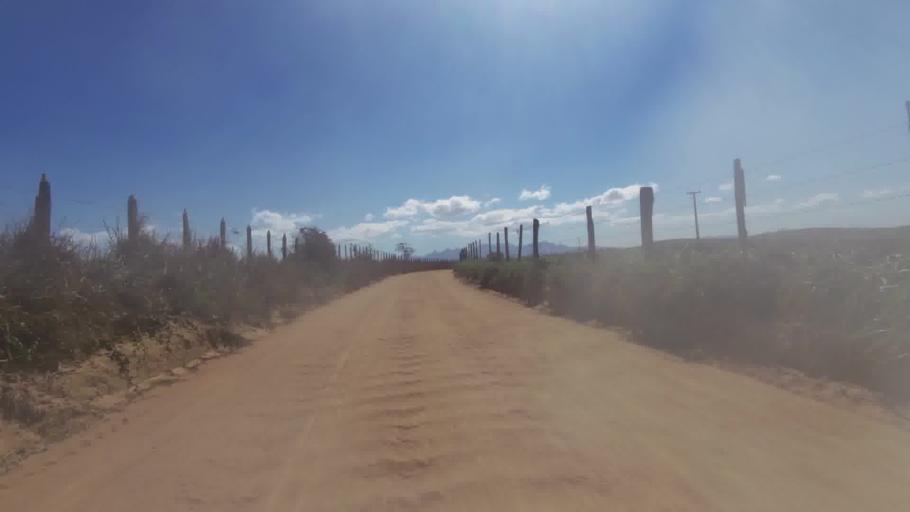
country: BR
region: Espirito Santo
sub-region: Marataizes
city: Marataizes
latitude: -21.1564
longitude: -40.9805
